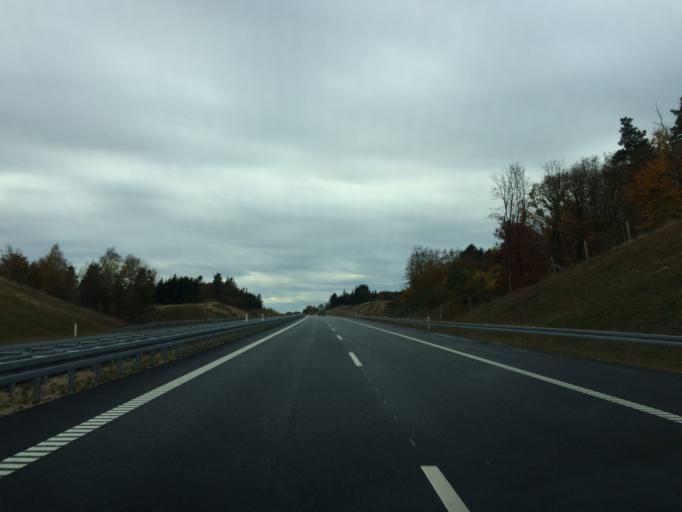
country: DK
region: Central Jutland
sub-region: Silkeborg Kommune
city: Silkeborg
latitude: 56.1776
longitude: 9.4802
